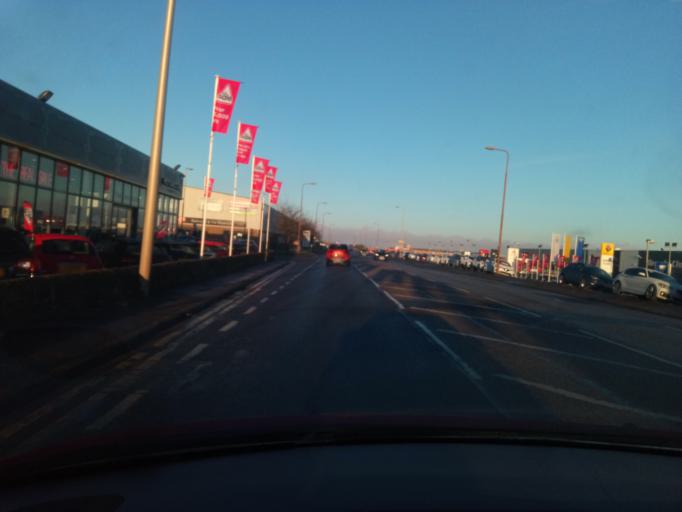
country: GB
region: Scotland
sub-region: West Lothian
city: Seafield
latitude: 55.9619
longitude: -3.1277
